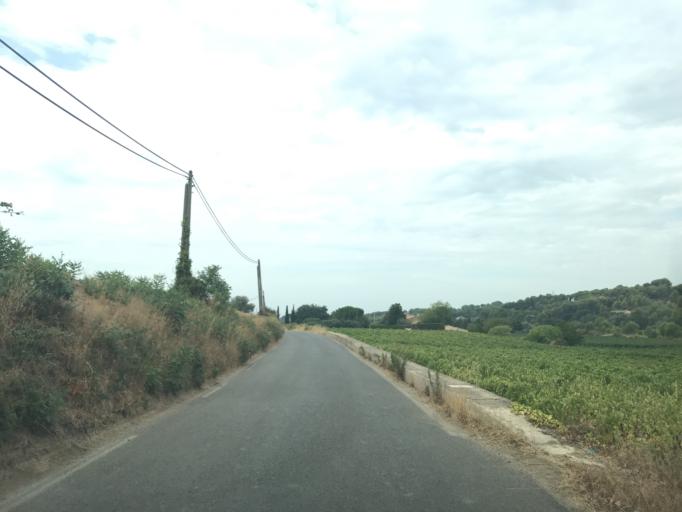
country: FR
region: Provence-Alpes-Cote d'Azur
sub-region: Departement du Var
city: Saint-Cyr-sur-Mer
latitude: 43.1866
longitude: 5.7420
